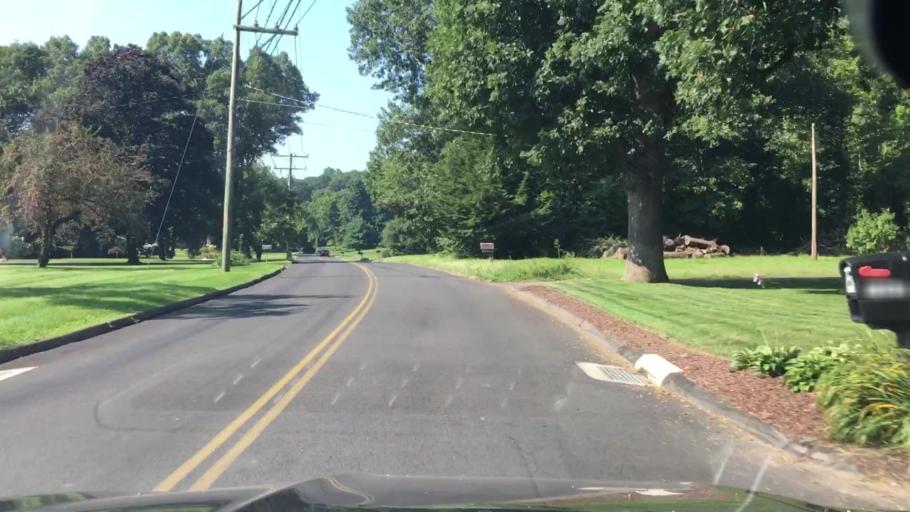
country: US
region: Connecticut
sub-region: New Haven County
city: Cheshire Village
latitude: 41.5373
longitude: -72.9047
